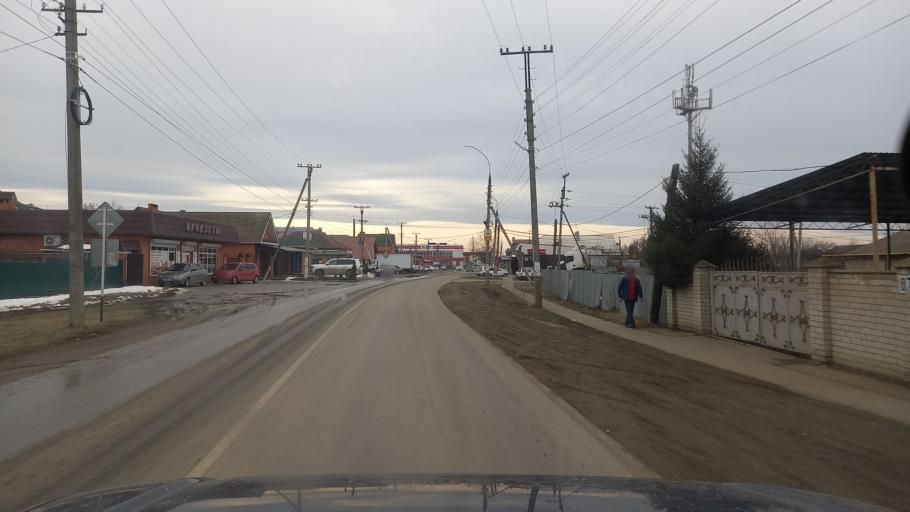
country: RU
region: Krasnodarskiy
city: Belorechensk
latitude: 44.7725
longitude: 39.8656
